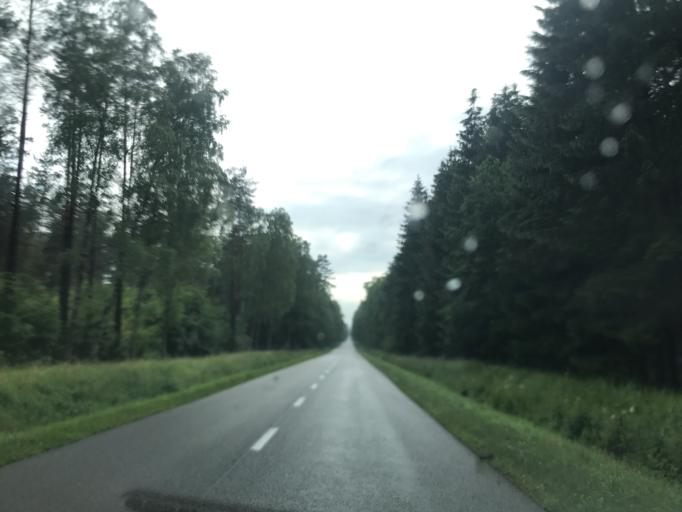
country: PL
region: West Pomeranian Voivodeship
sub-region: Powiat bialogardzki
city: Tychowo
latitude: 53.9429
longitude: 16.3104
